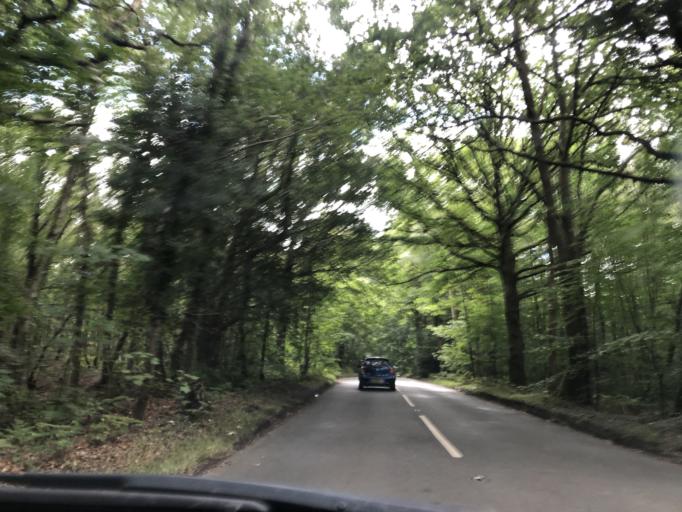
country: GB
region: England
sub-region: Kent
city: Westerham
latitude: 51.2558
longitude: 0.0797
